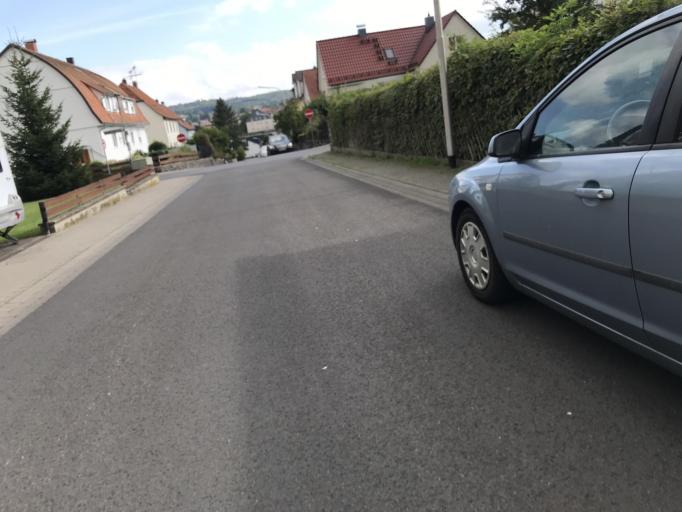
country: DE
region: Hesse
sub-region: Regierungsbezirk Giessen
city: Lauterbach
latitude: 50.6366
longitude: 9.3886
